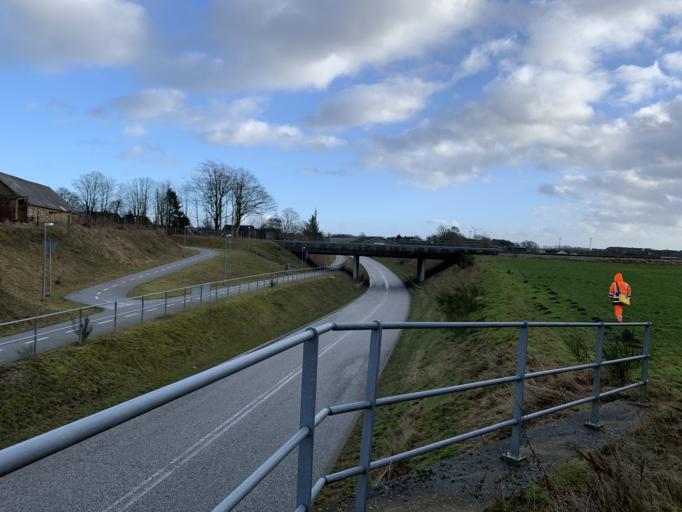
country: DK
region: North Denmark
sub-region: Mariagerfjord Kommune
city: Arden
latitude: 56.7088
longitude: 9.8376
